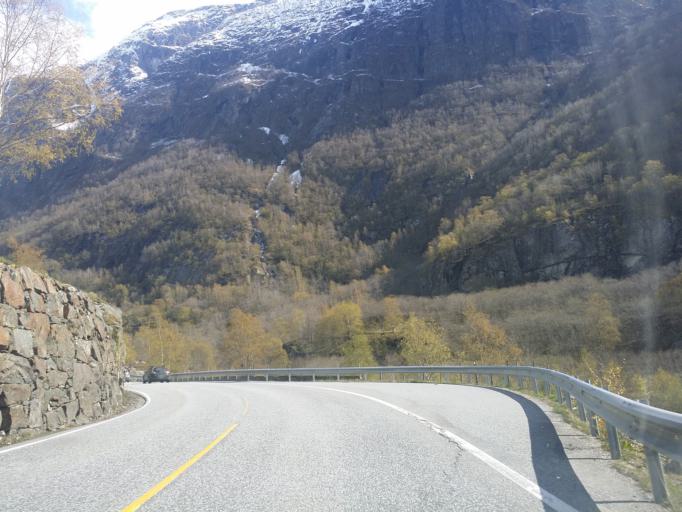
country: NO
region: Hordaland
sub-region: Eidfjord
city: Eidfjord
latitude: 60.4175
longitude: 7.1447
